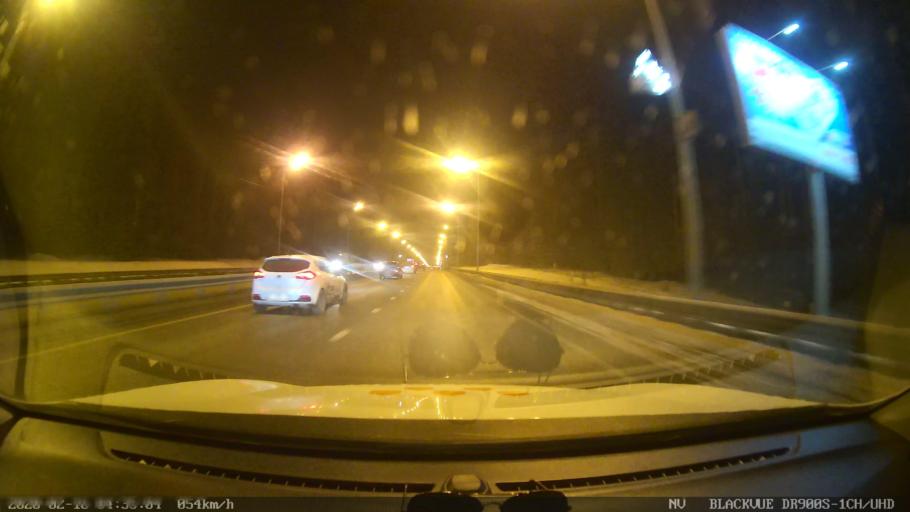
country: RU
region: Tatarstan
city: Staroye Arakchino
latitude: 55.8304
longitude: 48.9897
